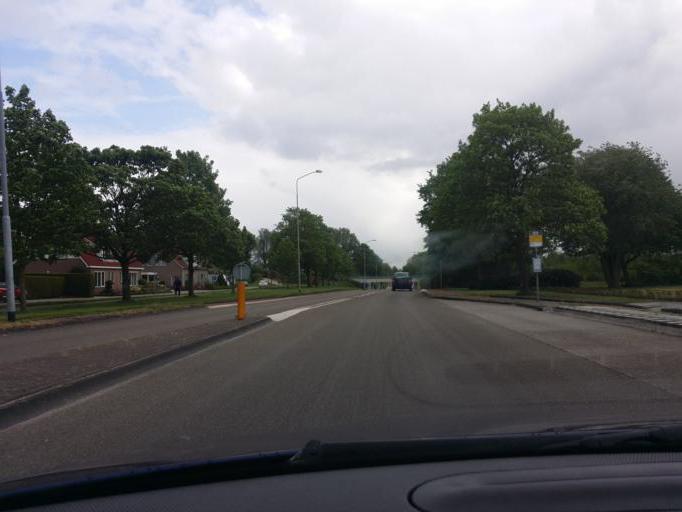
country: NL
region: Groningen
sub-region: Gemeente Hoogezand-Sappemeer
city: Hoogezand
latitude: 53.1626
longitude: 6.7393
